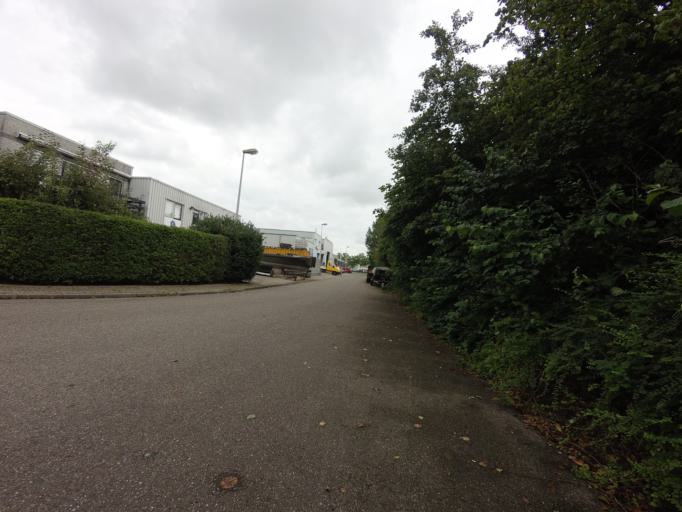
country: NL
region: North Holland
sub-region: Gemeente Purmerend
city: Purmerend
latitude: 52.5143
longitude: 4.9902
